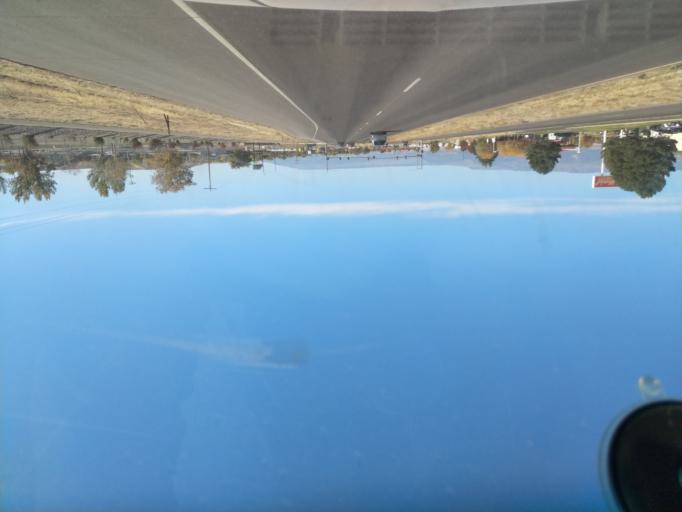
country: US
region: Colorado
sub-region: Mesa County
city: Orchard Mesa
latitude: 39.0403
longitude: -108.5408
